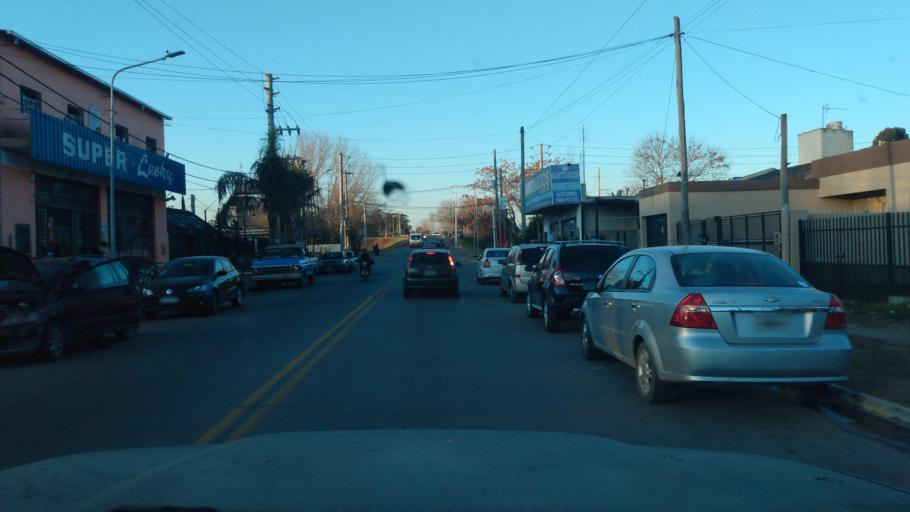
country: AR
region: Buenos Aires
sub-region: Partido de General Rodriguez
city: General Rodriguez
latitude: -34.5974
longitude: -58.9393
